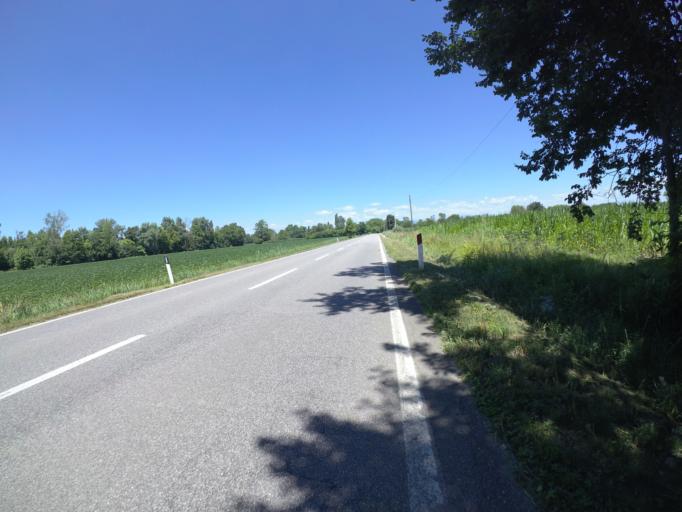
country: IT
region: Friuli Venezia Giulia
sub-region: Provincia di Udine
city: Talmassons
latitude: 45.9209
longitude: 13.0855
